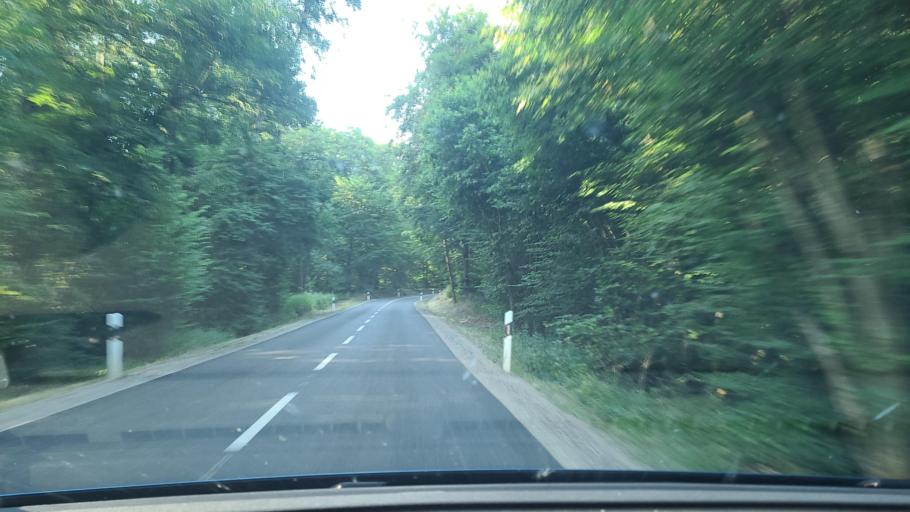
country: LU
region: Luxembourg
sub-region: Canton de Capellen
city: Dippach
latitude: 49.6011
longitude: 5.9905
